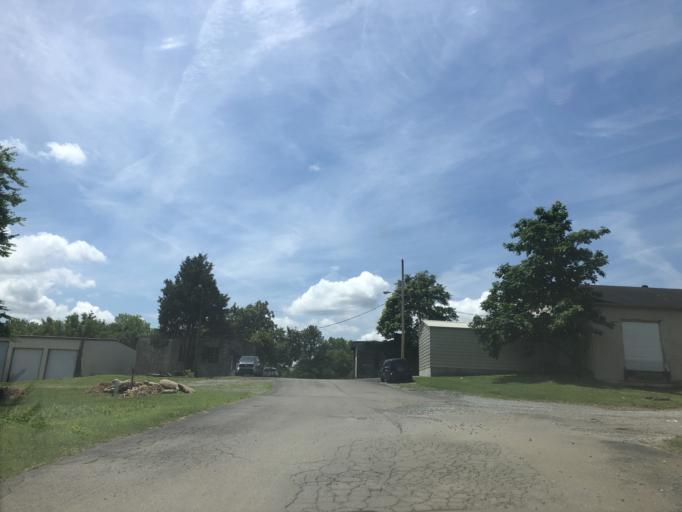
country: US
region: Tennessee
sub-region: Davidson County
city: Lakewood
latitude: 36.2546
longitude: -86.6774
